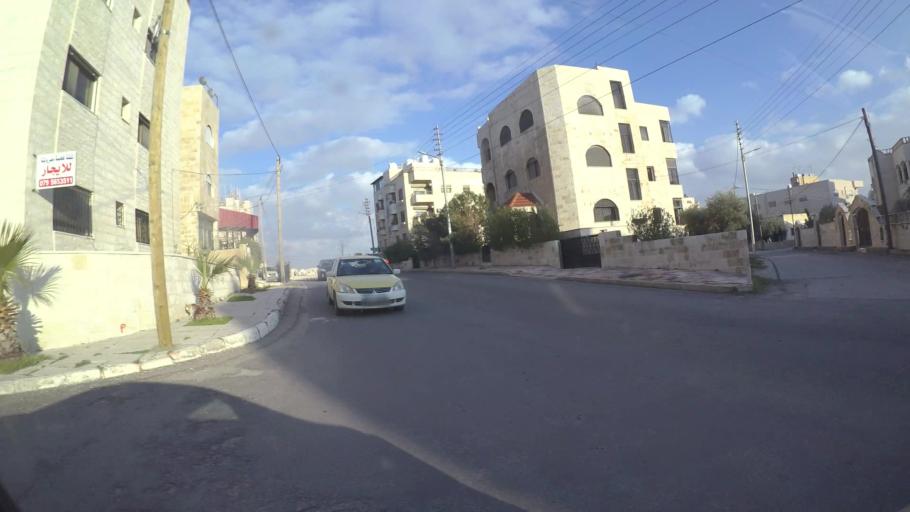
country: JO
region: Amman
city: Al Jubayhah
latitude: 31.9946
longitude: 35.8674
